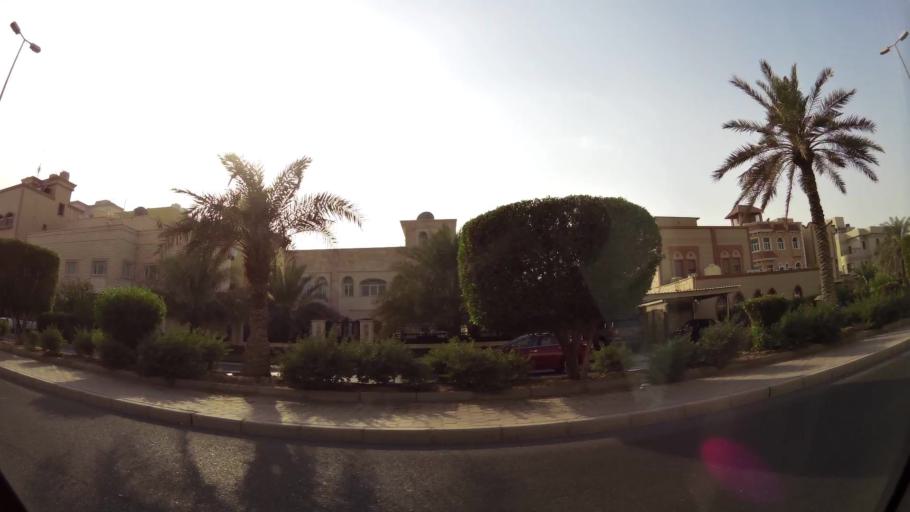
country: KW
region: Muhafazat Hawalli
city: Hawalli
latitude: 29.3245
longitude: 47.9978
